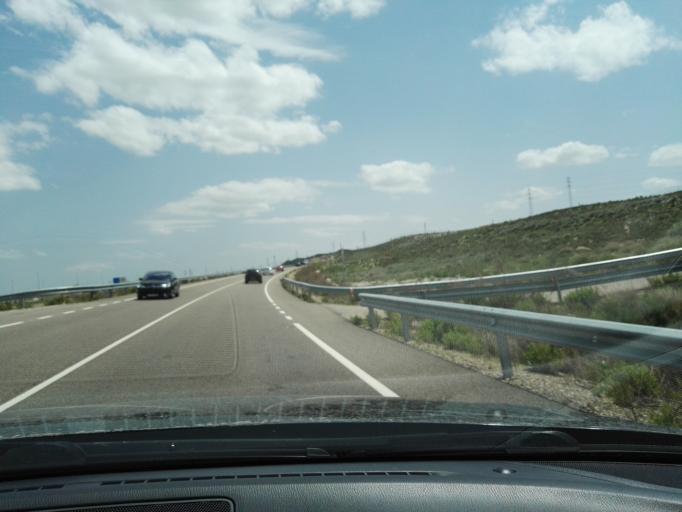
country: ES
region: Aragon
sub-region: Provincia de Zaragoza
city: Montecanal
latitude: 41.6208
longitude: -0.9722
